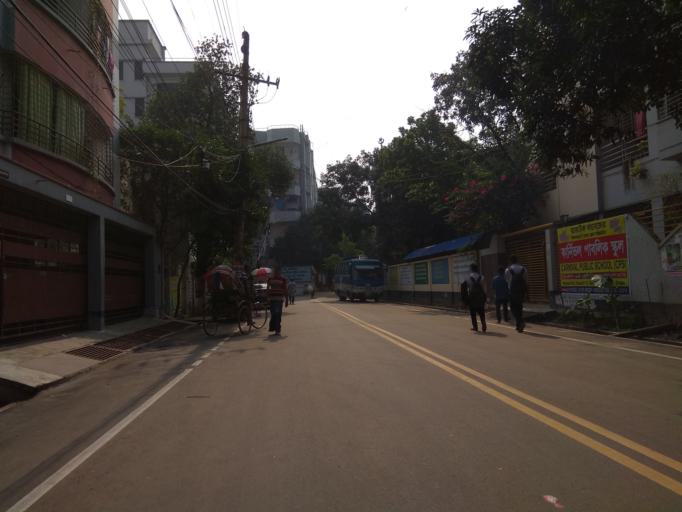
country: BD
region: Dhaka
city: Tungi
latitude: 23.8629
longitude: 90.3903
